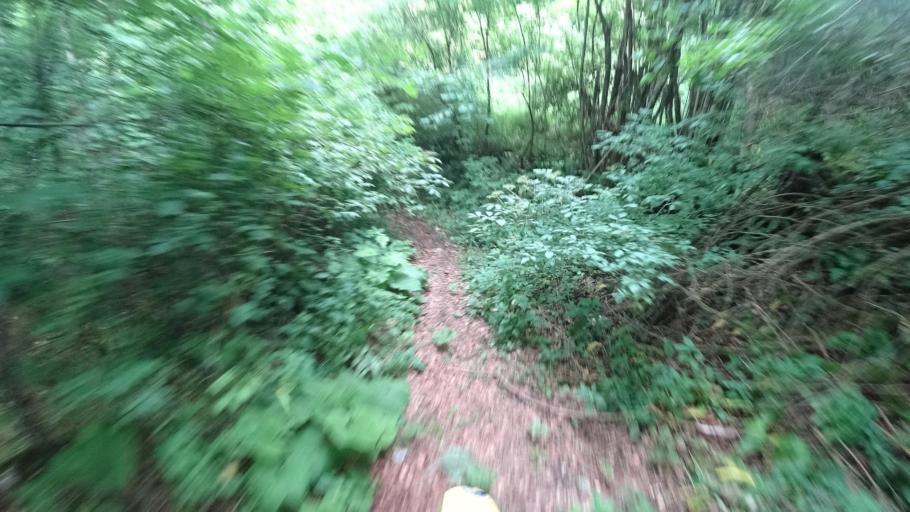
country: HR
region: Licko-Senjska
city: Jezerce
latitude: 44.9233
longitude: 15.6235
